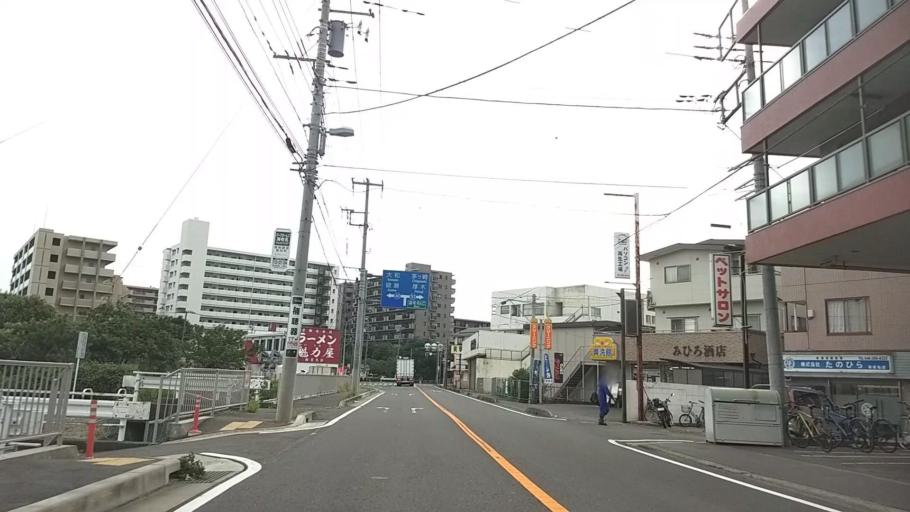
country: JP
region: Kanagawa
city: Atsugi
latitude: 35.4519
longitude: 139.3811
